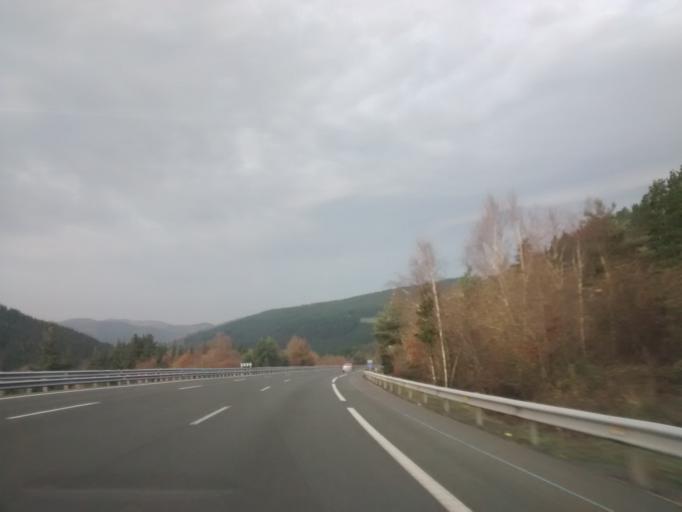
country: ES
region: Basque Country
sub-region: Provincia de Alava
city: Lezama
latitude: 43.0224
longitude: -2.9123
